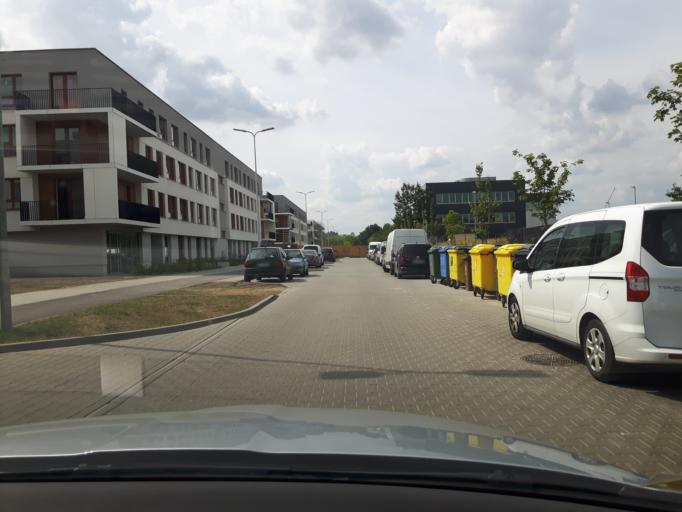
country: PL
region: Masovian Voivodeship
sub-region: Warszawa
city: Ursynow
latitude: 52.1518
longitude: 21.0048
